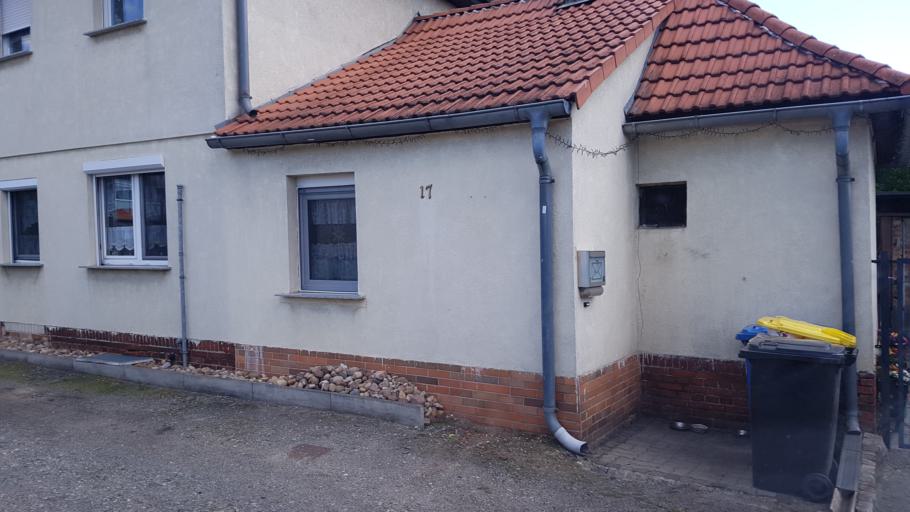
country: DE
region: Brandenburg
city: Grossraschen
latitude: 51.5800
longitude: 14.0048
